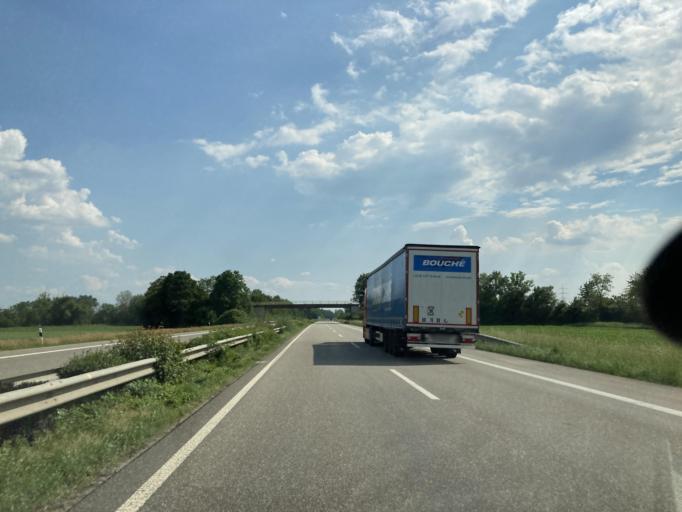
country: DE
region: Rheinland-Pfalz
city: Neupotz
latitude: 49.1114
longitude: 8.3058
